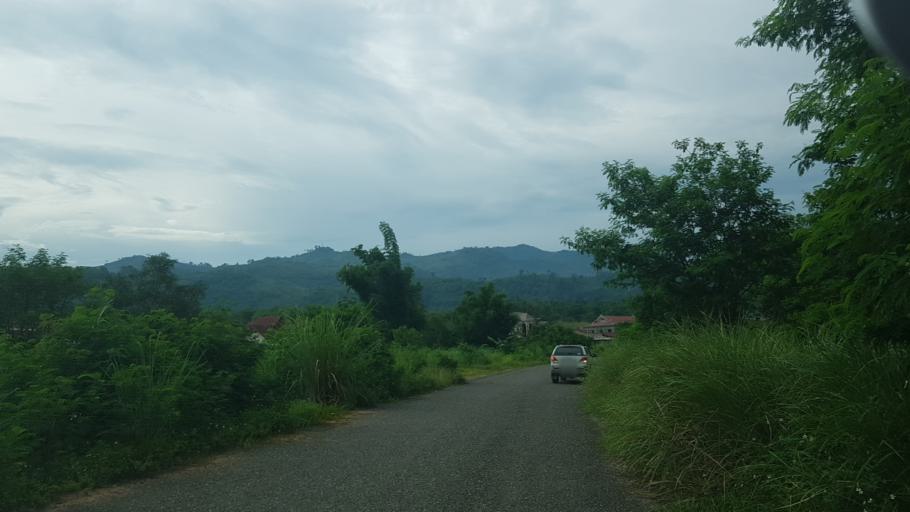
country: LA
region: Oudomxai
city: Muang Xay
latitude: 20.6956
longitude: 101.9899
